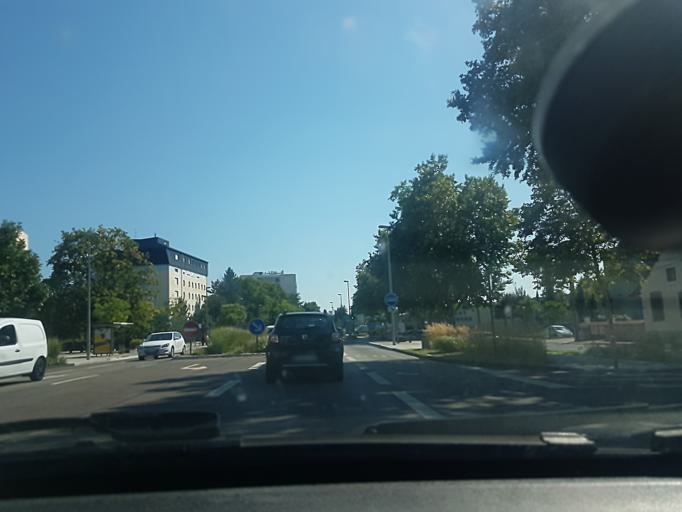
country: FR
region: Bourgogne
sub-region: Departement de Saone-et-Loire
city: Chalon-sur-Saone
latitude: 46.7929
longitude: 4.8636
